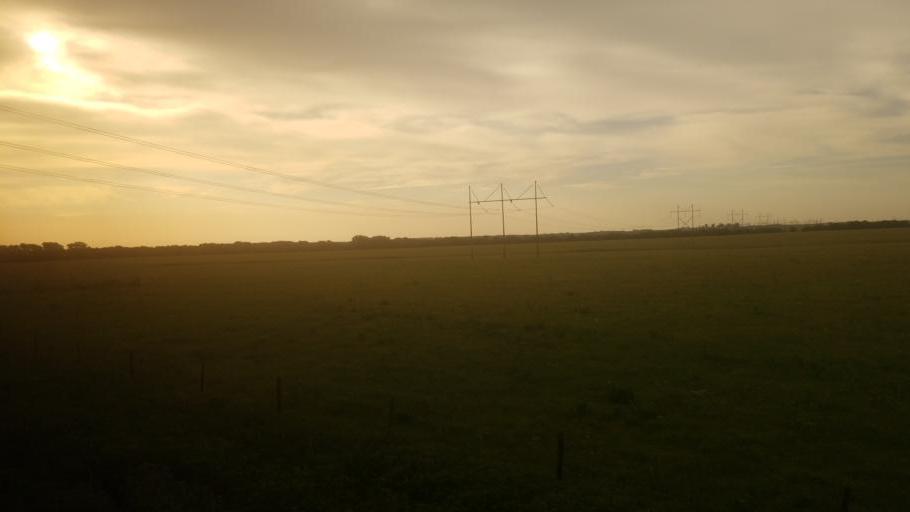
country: US
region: Kansas
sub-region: Lyon County
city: Emporia
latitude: 38.4566
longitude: -96.0879
